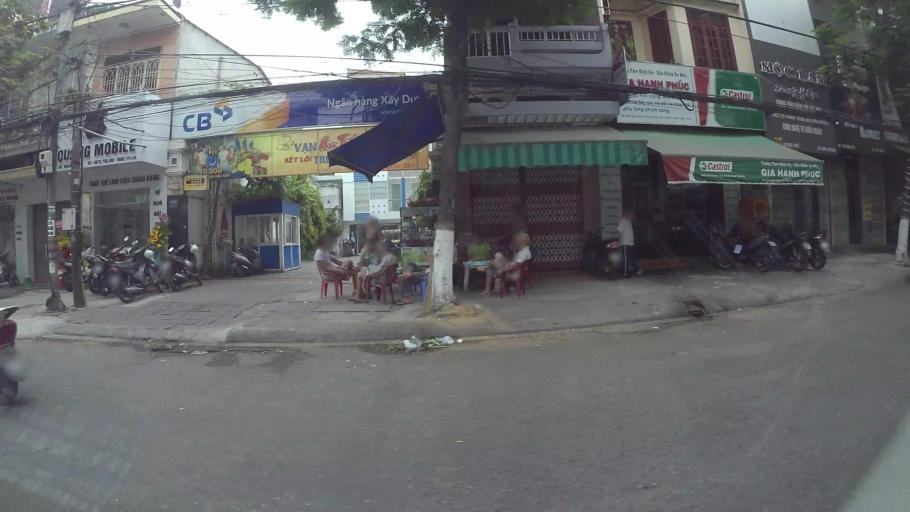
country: VN
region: Da Nang
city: Da Nang
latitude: 16.0545
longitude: 108.2175
